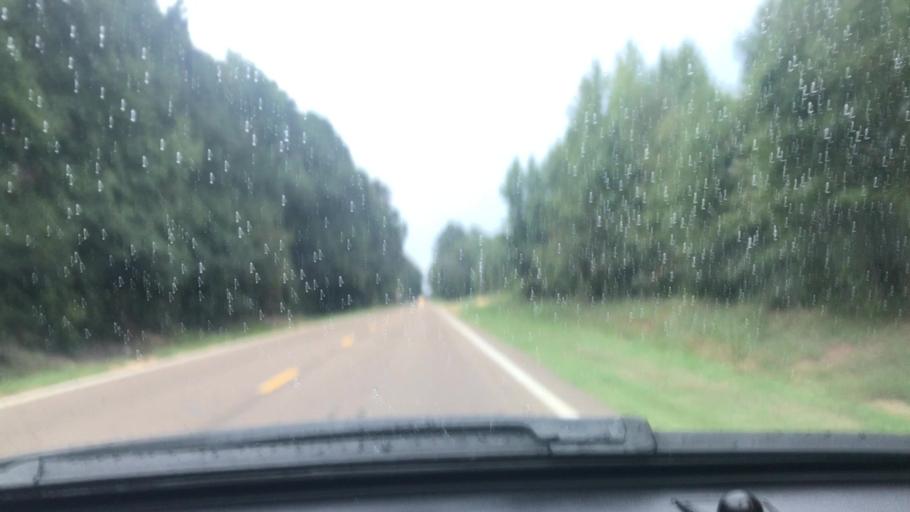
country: US
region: Mississippi
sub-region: Pike County
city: Summit
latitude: 31.3509
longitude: -90.6029
